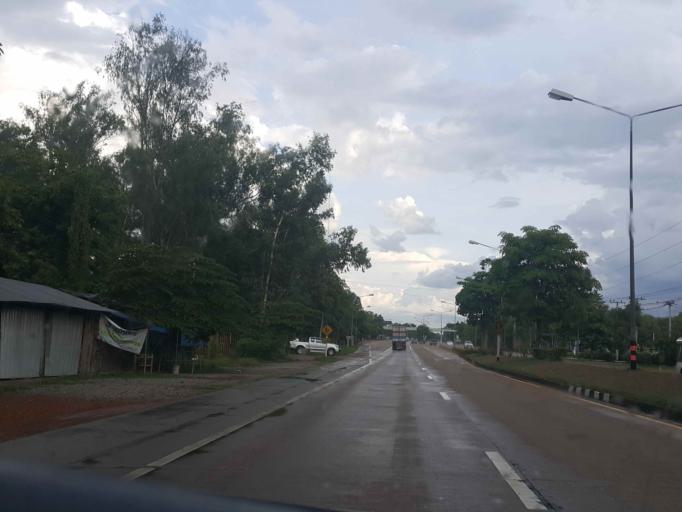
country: TH
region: Phrae
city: Den Chai
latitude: 17.9849
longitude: 100.0943
